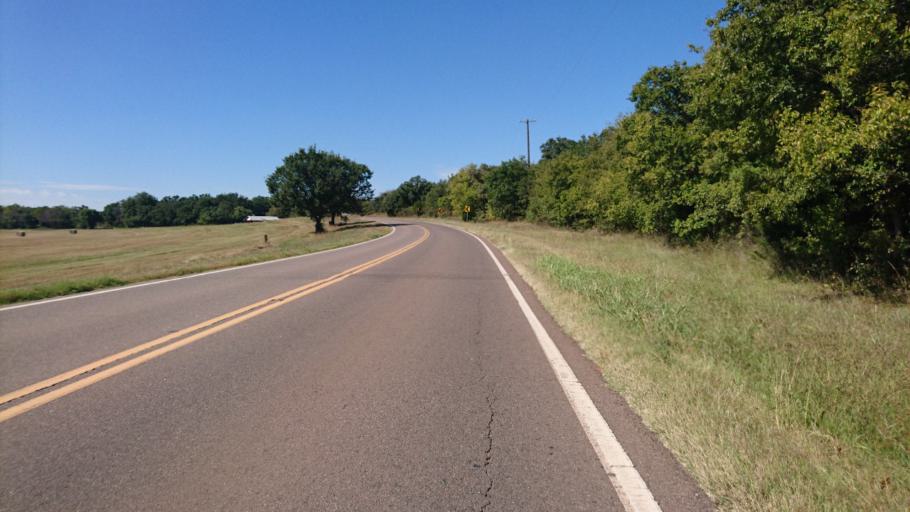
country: US
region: Oklahoma
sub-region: Oklahoma County
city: Luther
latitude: 35.6671
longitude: -97.2440
